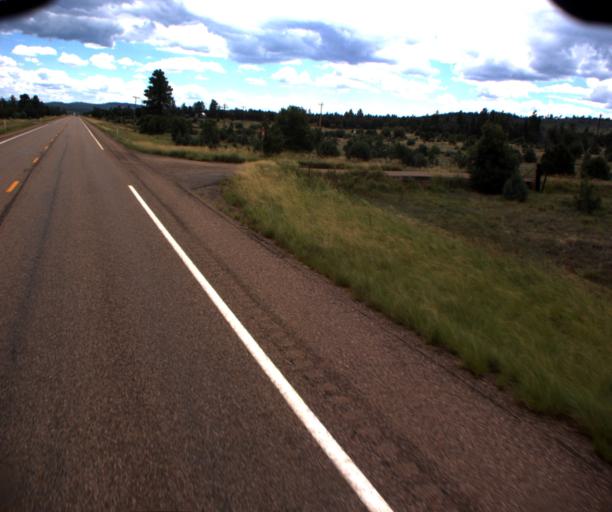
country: US
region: Arizona
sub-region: Navajo County
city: Linden
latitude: 34.3285
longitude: -110.2621
